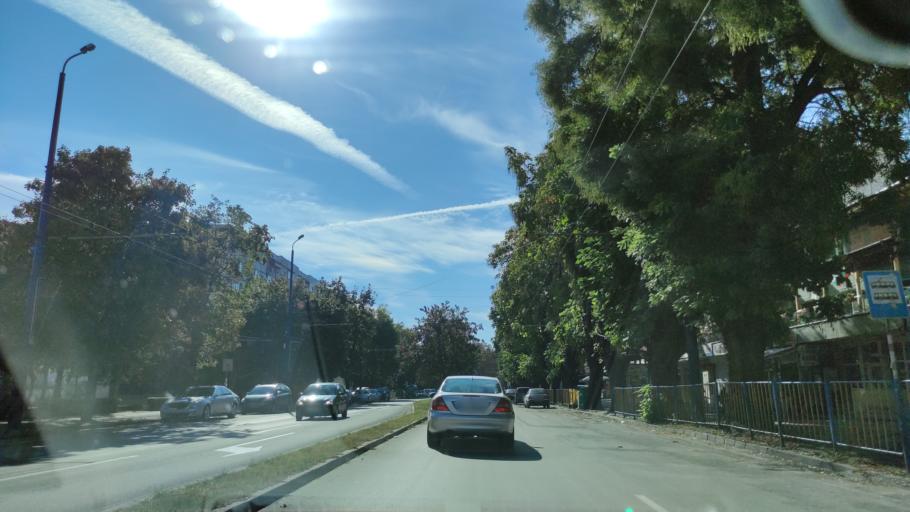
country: BG
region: Pazardzhik
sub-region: Obshtina Pazardzhik
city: Pazardzhik
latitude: 42.2028
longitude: 24.3312
